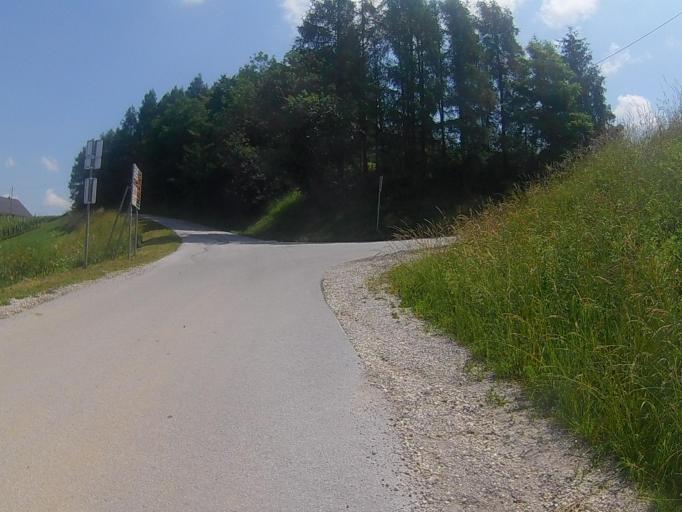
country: SI
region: Pesnica
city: Pesnica pri Mariboru
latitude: 46.5720
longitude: 15.7016
